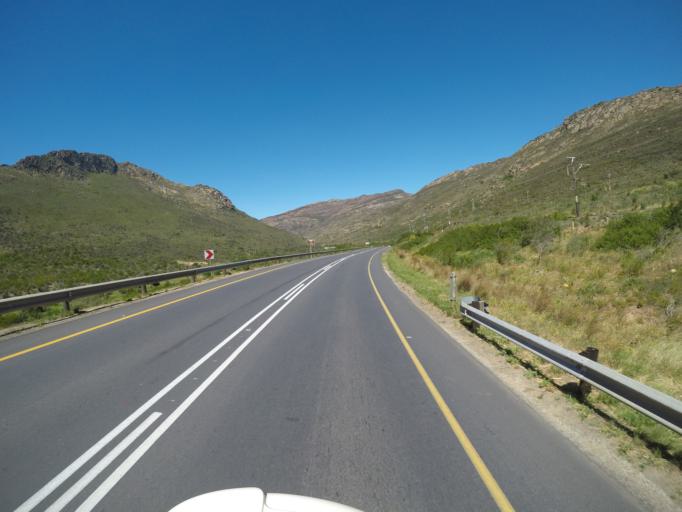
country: ZA
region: Western Cape
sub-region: Cape Winelands District Municipality
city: Ceres
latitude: -33.3045
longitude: 19.0689
